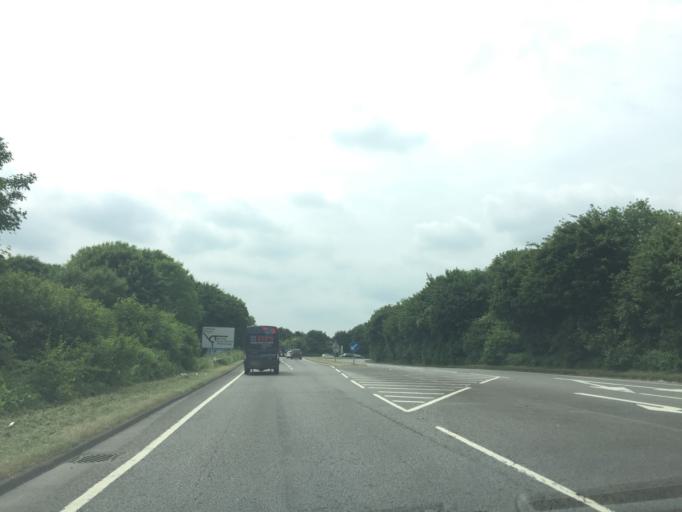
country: GB
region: England
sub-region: Hampshire
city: Kings Worthy
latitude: 51.0600
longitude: -1.2891
